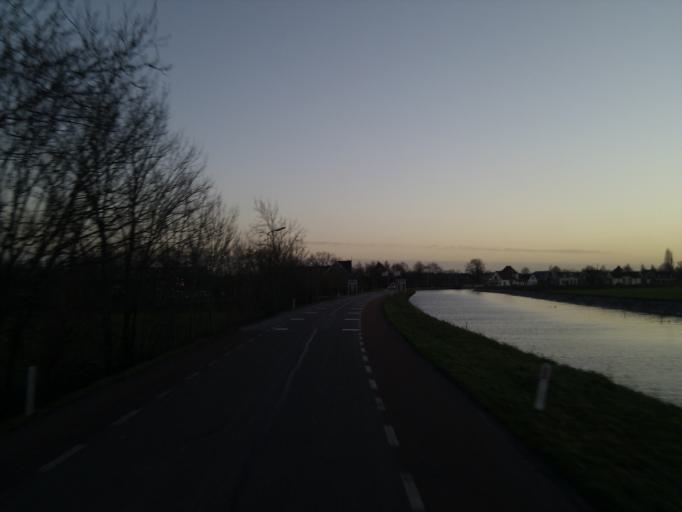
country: NL
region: Utrecht
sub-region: Stichtse Vecht
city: Vreeland
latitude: 52.2528
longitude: 4.9935
